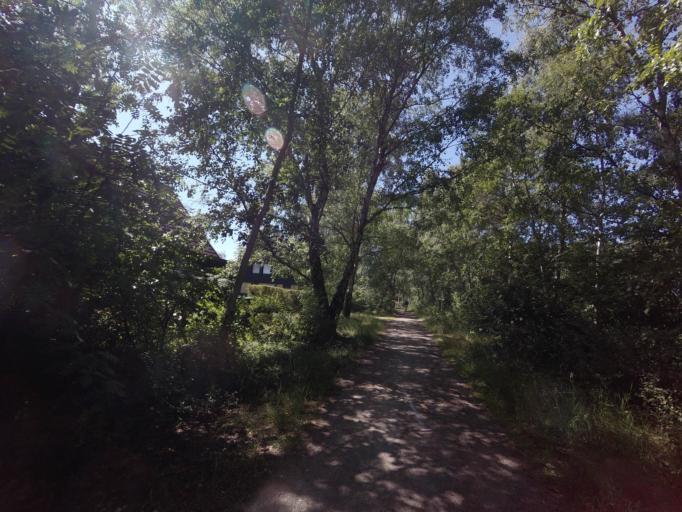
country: SE
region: Skane
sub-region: Vellinge Kommun
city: Skanor med Falsterbo
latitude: 55.4046
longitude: 12.8605
